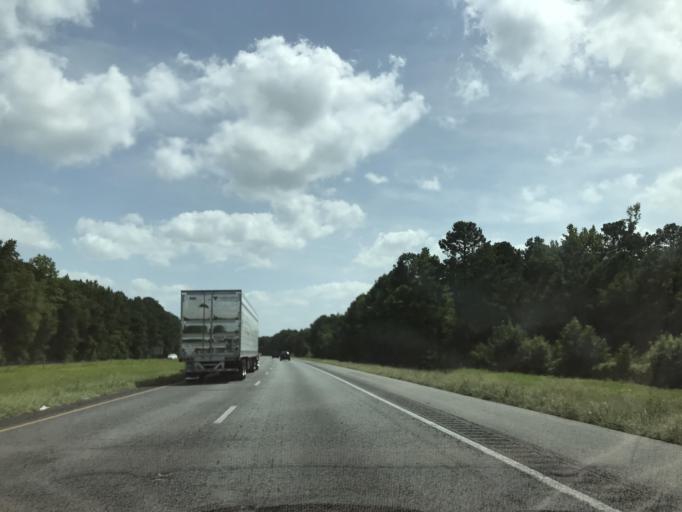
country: US
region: North Carolina
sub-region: Duplin County
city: Warsaw
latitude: 34.9789
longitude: -78.1285
